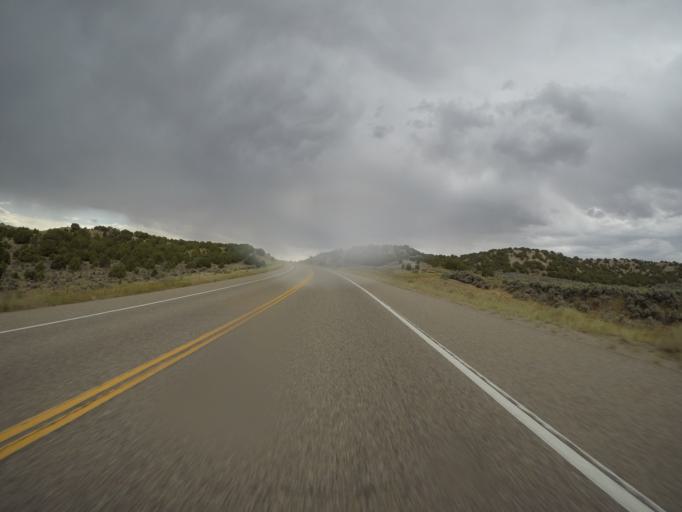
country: US
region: Colorado
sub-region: Rio Blanco County
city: Meeker
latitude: 40.4099
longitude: -108.3358
